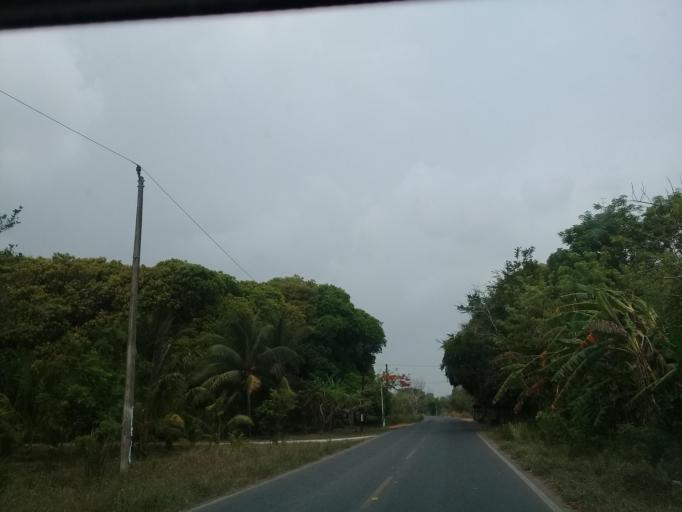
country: MX
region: Veracruz
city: El Tejar
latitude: 19.0548
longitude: -96.1947
